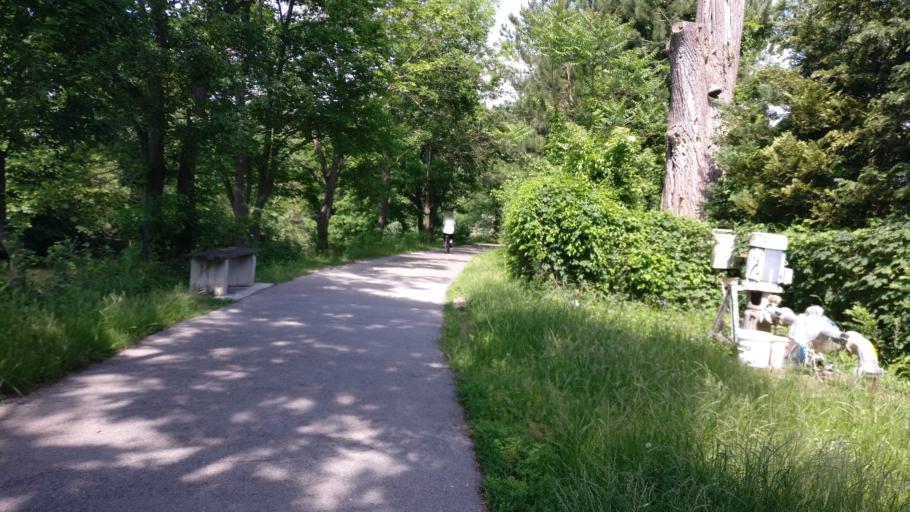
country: AT
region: Lower Austria
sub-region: Politischer Bezirk Baden
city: Trumau
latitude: 47.9860
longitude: 16.3345
